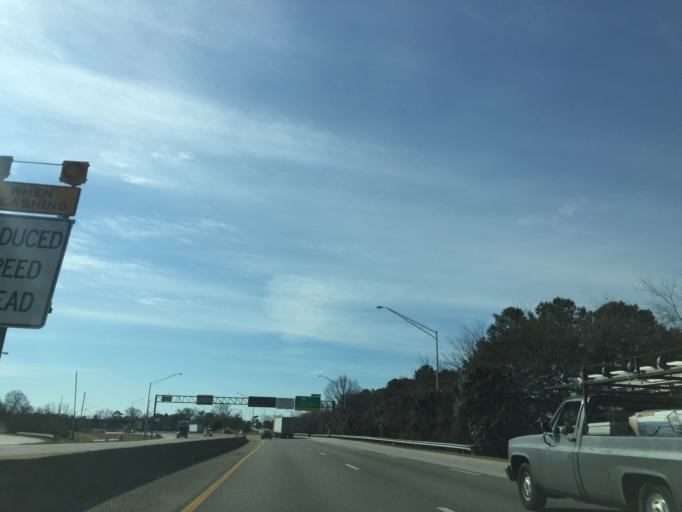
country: US
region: Virginia
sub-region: City of Hampton
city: East Hampton
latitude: 37.0195
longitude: -76.3287
